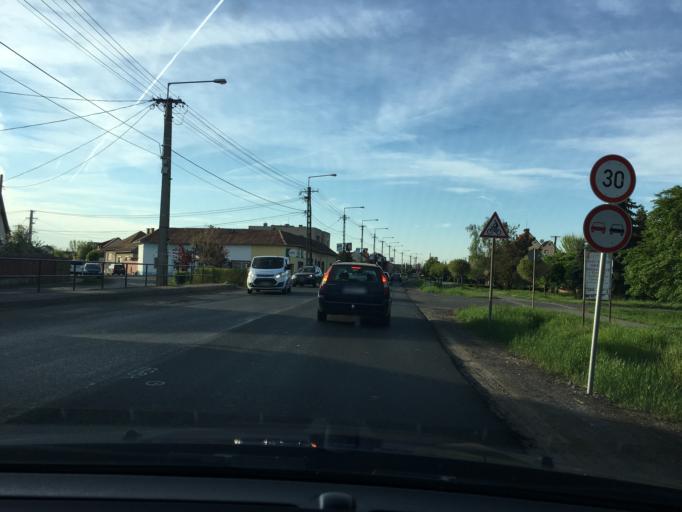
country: HU
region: Hajdu-Bihar
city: Berettyoujfalu
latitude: 47.2281
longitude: 21.5332
